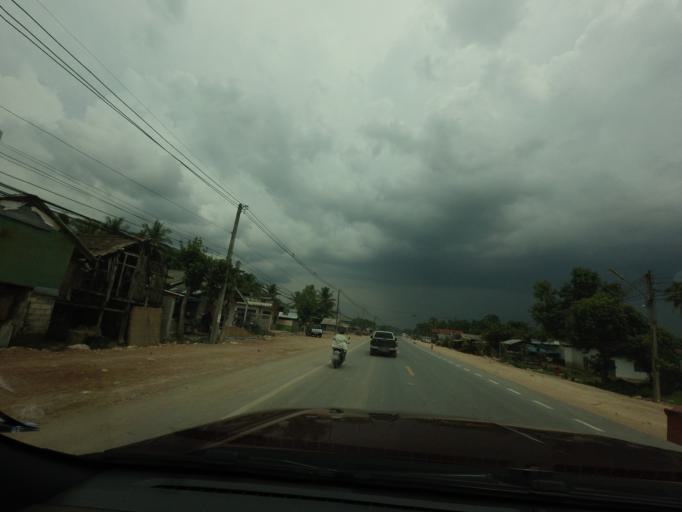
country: TH
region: Yala
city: Krong Pi Nang
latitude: 6.4435
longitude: 101.2774
